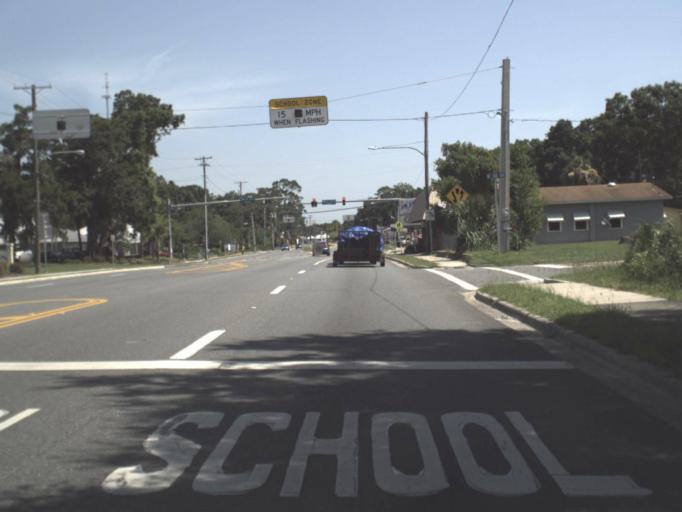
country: US
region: Florida
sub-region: Levy County
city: Chiefland
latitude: 29.4809
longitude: -82.8596
